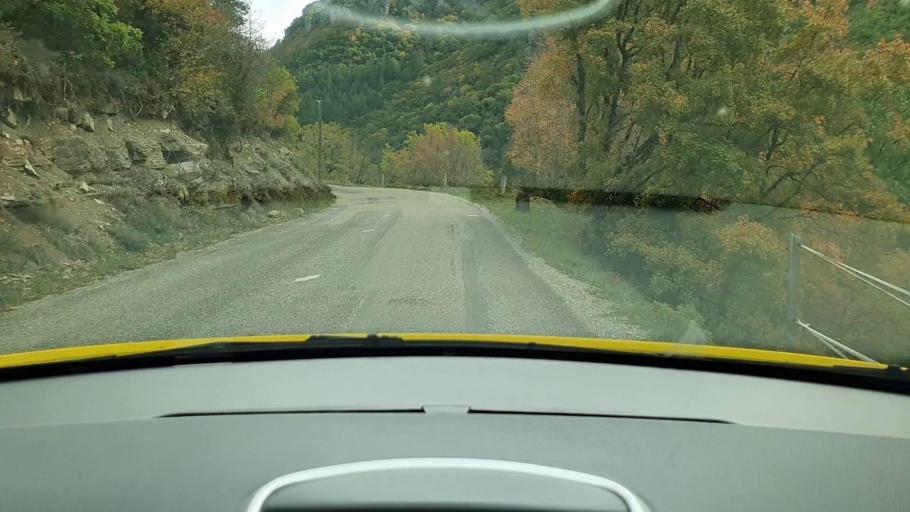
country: FR
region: Languedoc-Roussillon
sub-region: Departement de la Lozere
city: Meyrueis
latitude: 44.0757
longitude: 3.3634
